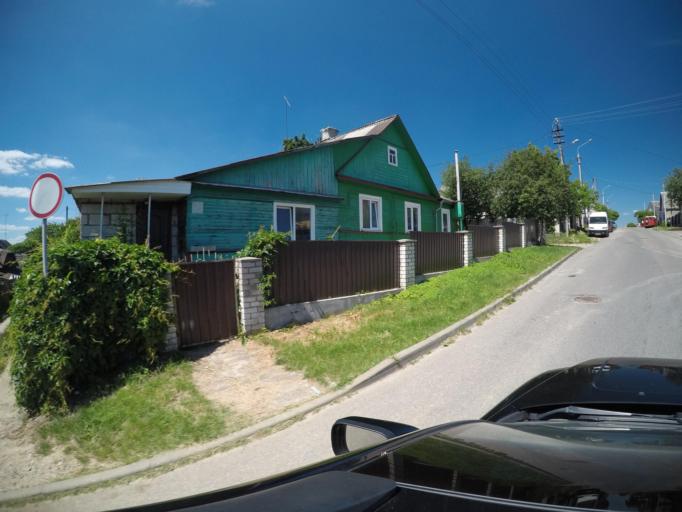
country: BY
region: Grodnenskaya
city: Hrodna
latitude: 53.6911
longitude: 23.8179
